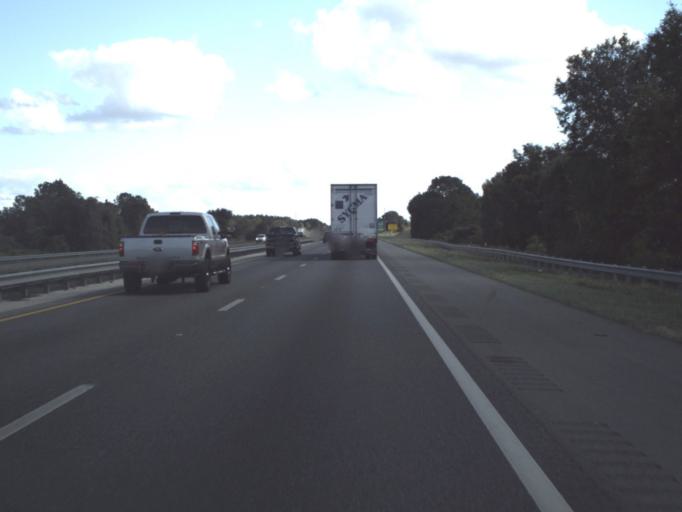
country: US
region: Florida
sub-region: Lake County
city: Hawthorne
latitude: 28.6892
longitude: -81.8692
